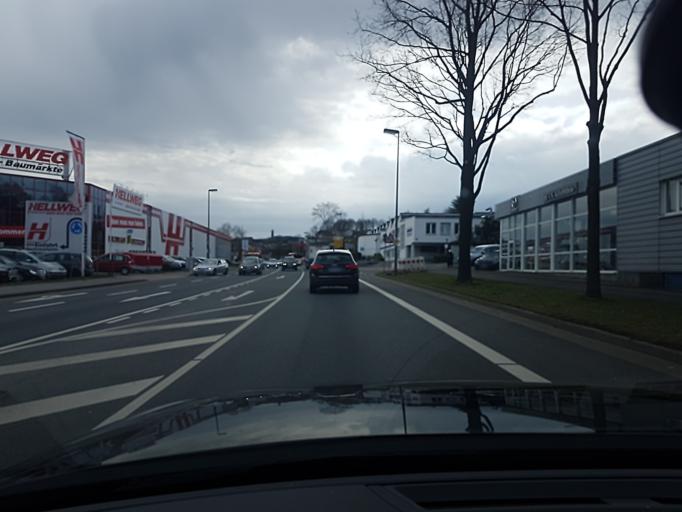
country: DE
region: North Rhine-Westphalia
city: Iserlohn
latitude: 51.3956
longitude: 7.6923
